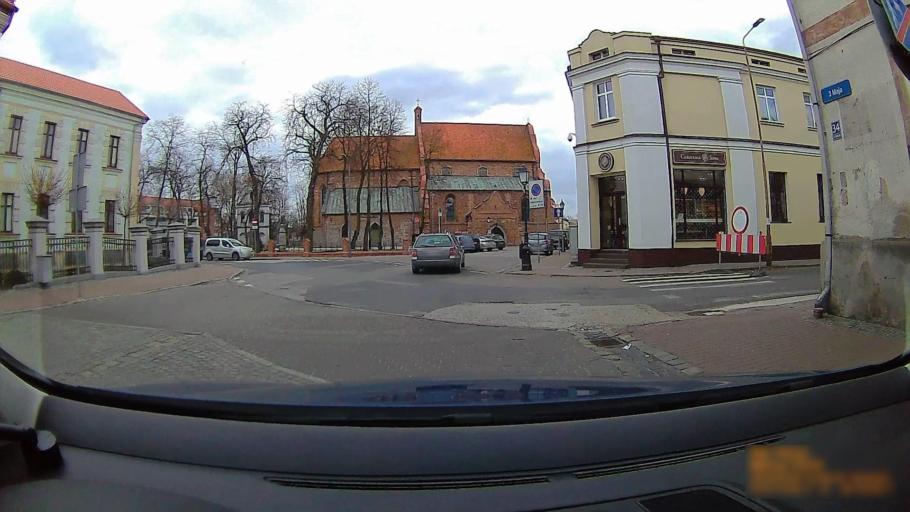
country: PL
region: Greater Poland Voivodeship
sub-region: Konin
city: Konin
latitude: 52.2100
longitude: 18.2545
